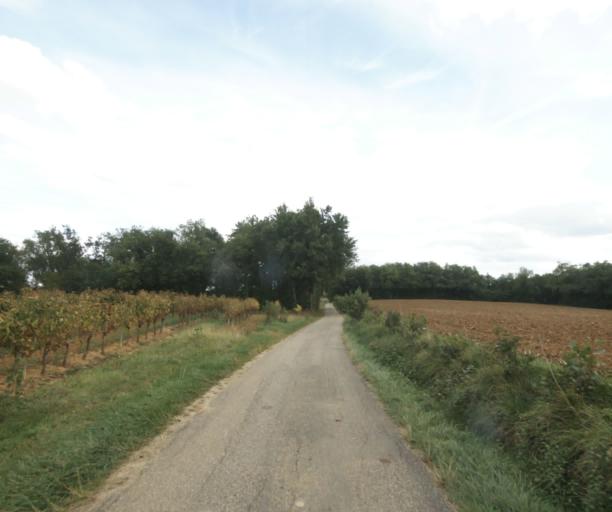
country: FR
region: Midi-Pyrenees
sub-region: Departement du Gers
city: Gondrin
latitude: 43.8668
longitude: 0.2555
